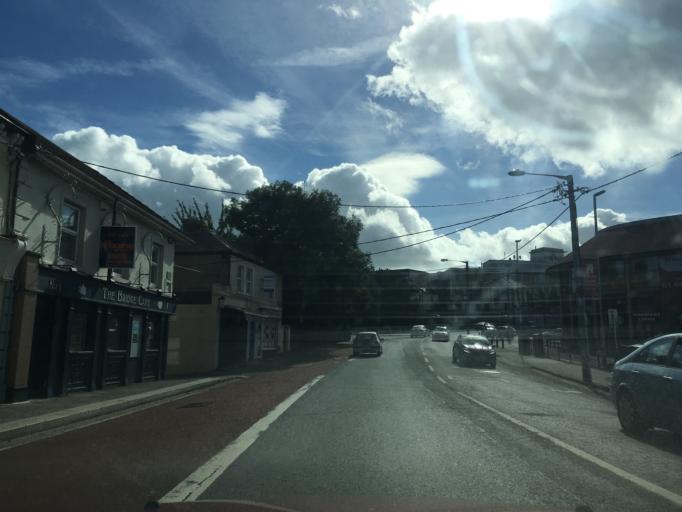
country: IE
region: Leinster
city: Little Bray
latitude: 53.2062
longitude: -6.1108
